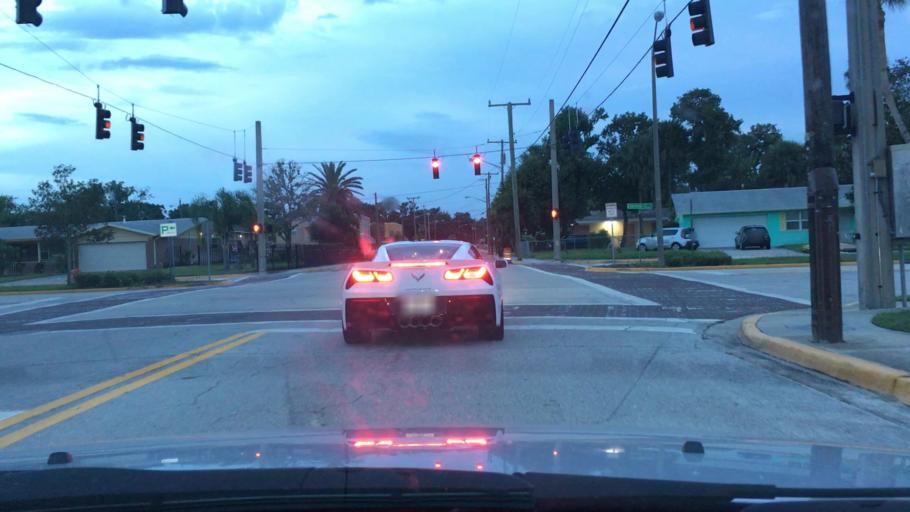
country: US
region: Florida
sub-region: Volusia County
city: Daytona Beach
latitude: 29.2110
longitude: -81.0330
